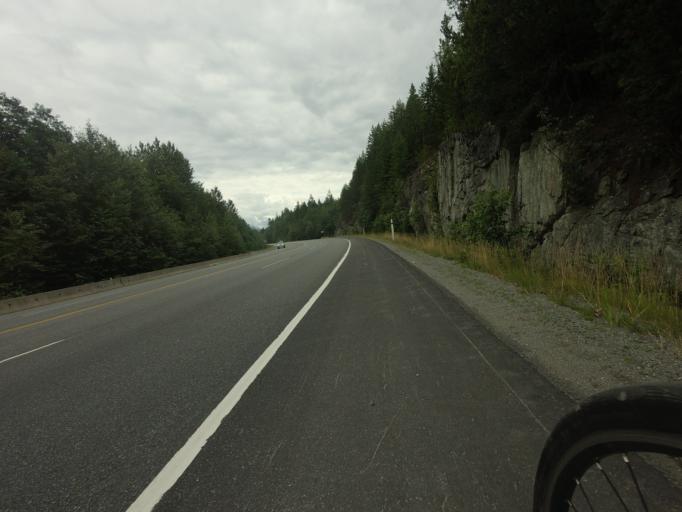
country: CA
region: British Columbia
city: Whistler
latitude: 49.8681
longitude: -123.1613
